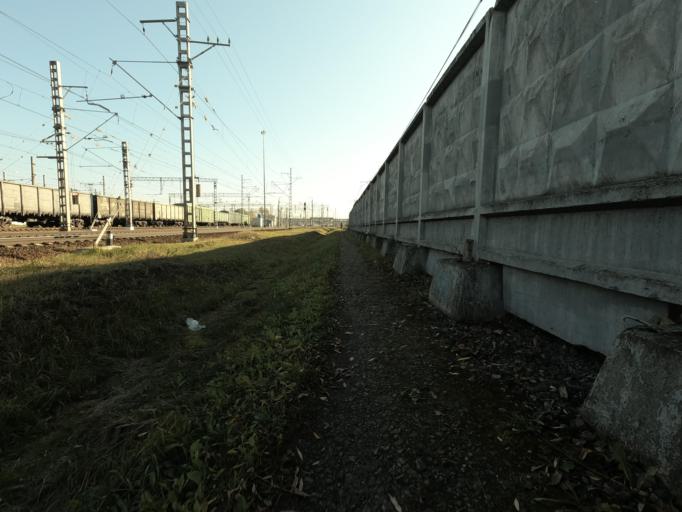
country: RU
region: St.-Petersburg
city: Obukhovo
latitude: 59.8519
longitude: 30.4492
